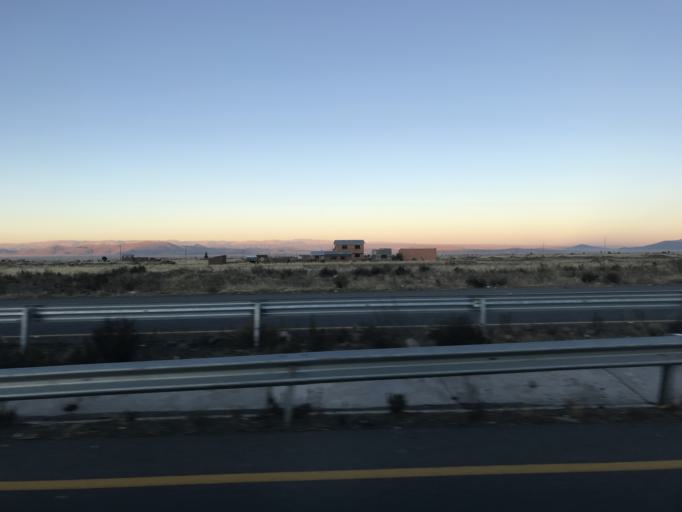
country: BO
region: La Paz
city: Batallas
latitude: -16.3659
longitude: -68.3899
